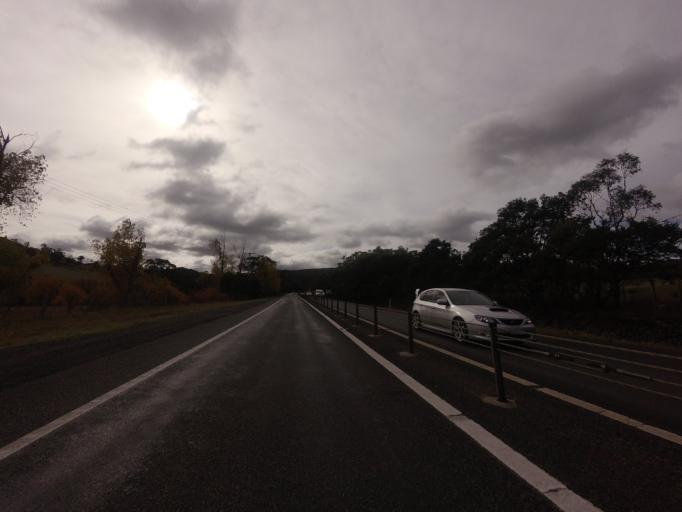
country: AU
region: Tasmania
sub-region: Brighton
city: Bridgewater
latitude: -42.5911
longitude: 147.2231
